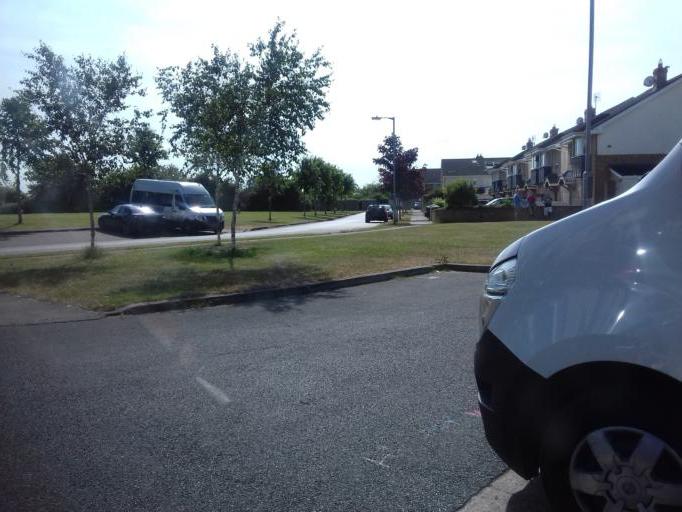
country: IE
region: Leinster
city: Lusk
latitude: 53.5243
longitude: -6.1774
